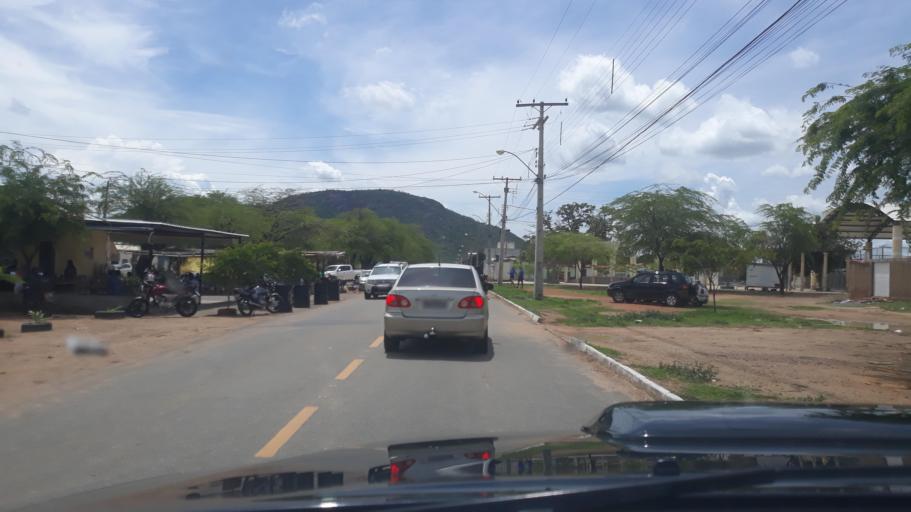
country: BR
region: Bahia
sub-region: Guanambi
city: Guanambi
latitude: -14.2857
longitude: -42.7123
